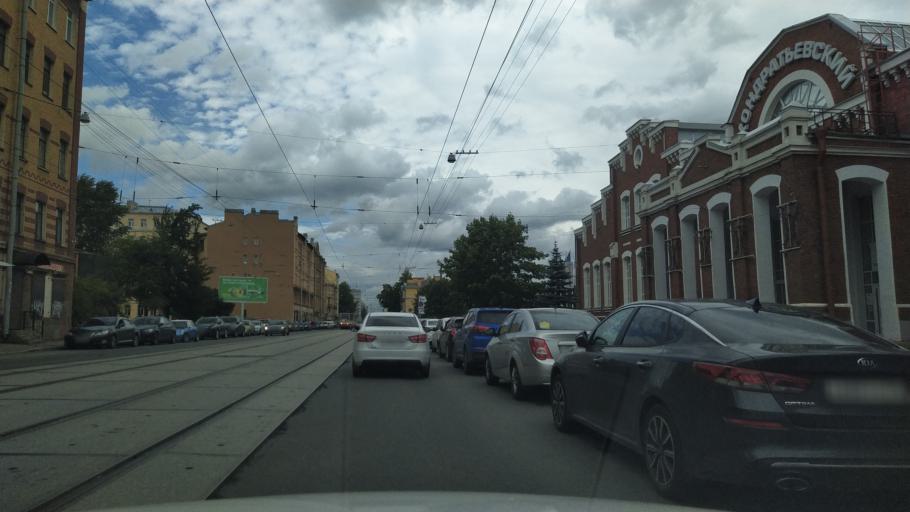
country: RU
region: Leningrad
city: Finlyandskiy
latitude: 59.9645
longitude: 30.3812
